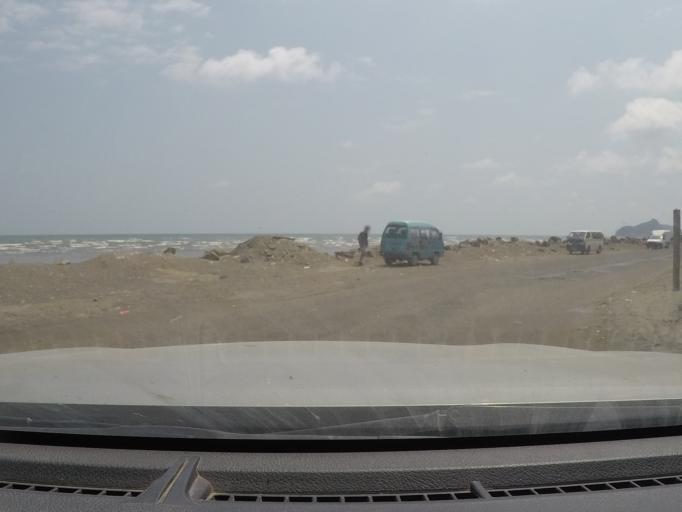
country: YE
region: Aden
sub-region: Khur Maksar
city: Khawr Maksar
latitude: 12.8142
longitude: 45.0434
